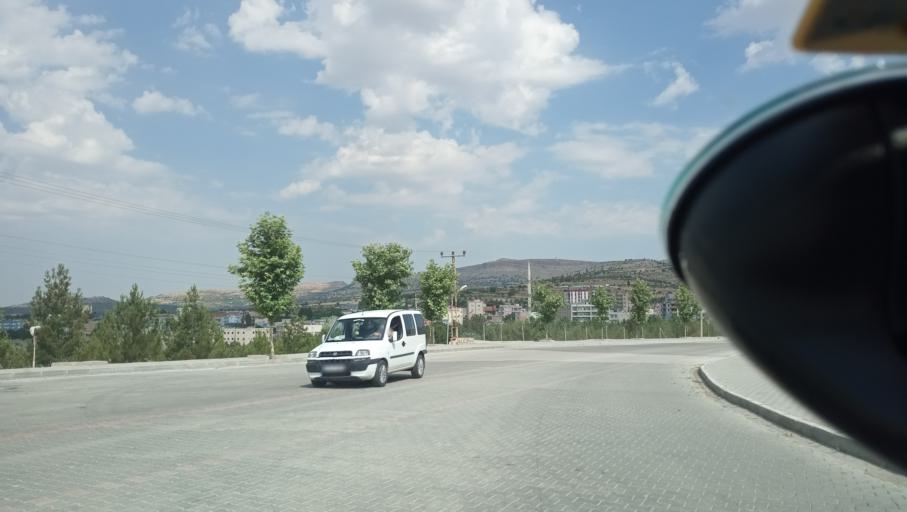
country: TR
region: Mardin
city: Kabala
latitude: 37.3433
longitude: 40.8045
